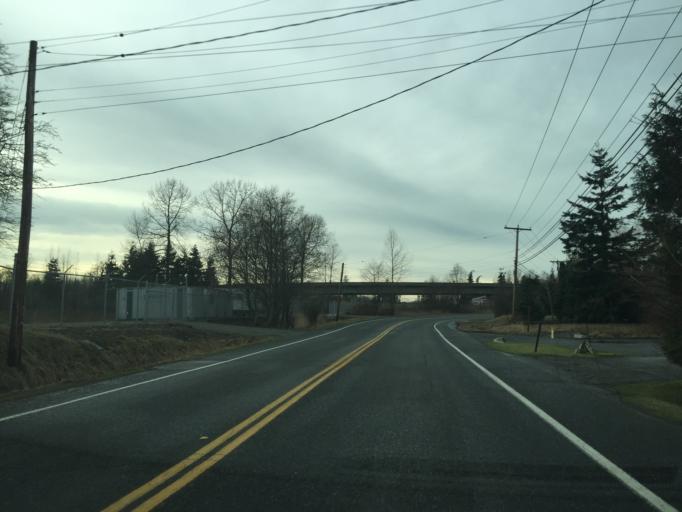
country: US
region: Washington
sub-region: Whatcom County
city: Marietta-Alderwood
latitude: 48.7896
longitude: -122.5164
